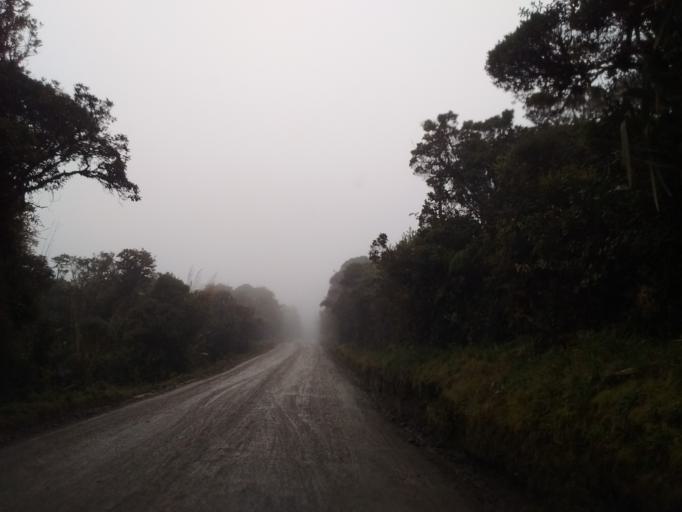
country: CO
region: Cauca
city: Paispamba
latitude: 2.1486
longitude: -76.4382
